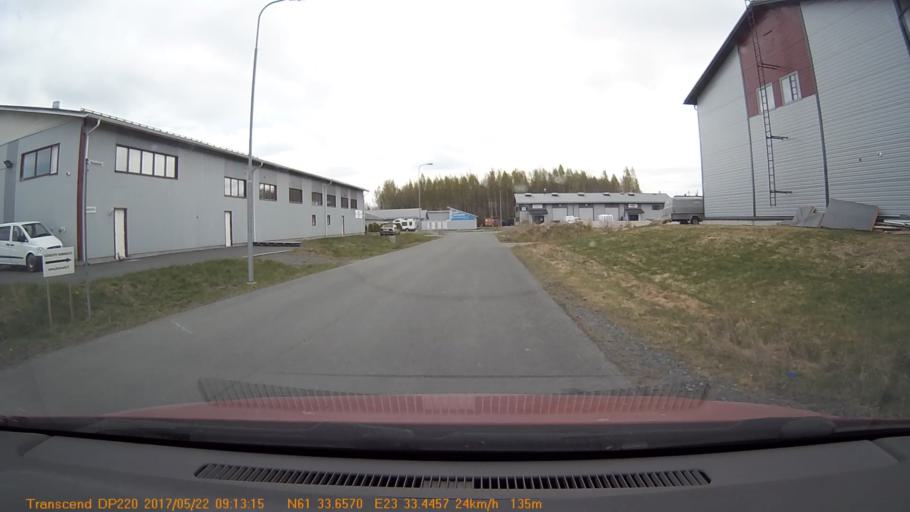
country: FI
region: Pirkanmaa
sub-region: Tampere
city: Yloejaervi
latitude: 61.5610
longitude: 23.5575
